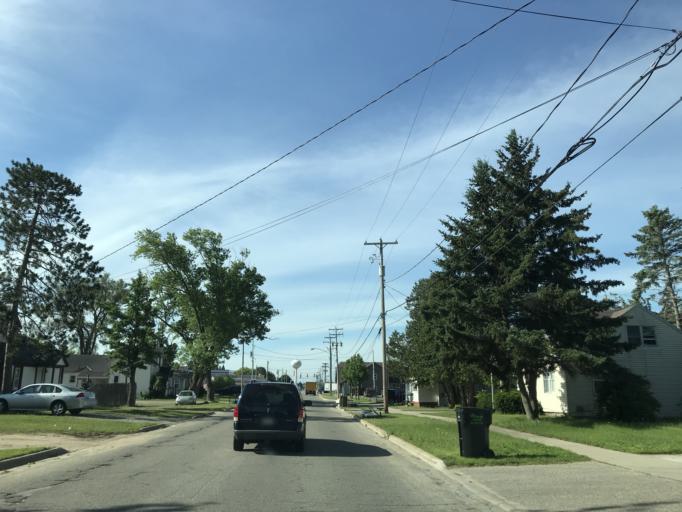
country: US
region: Michigan
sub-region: Otsego County
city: Gaylord
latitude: 45.0291
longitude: -84.6825
